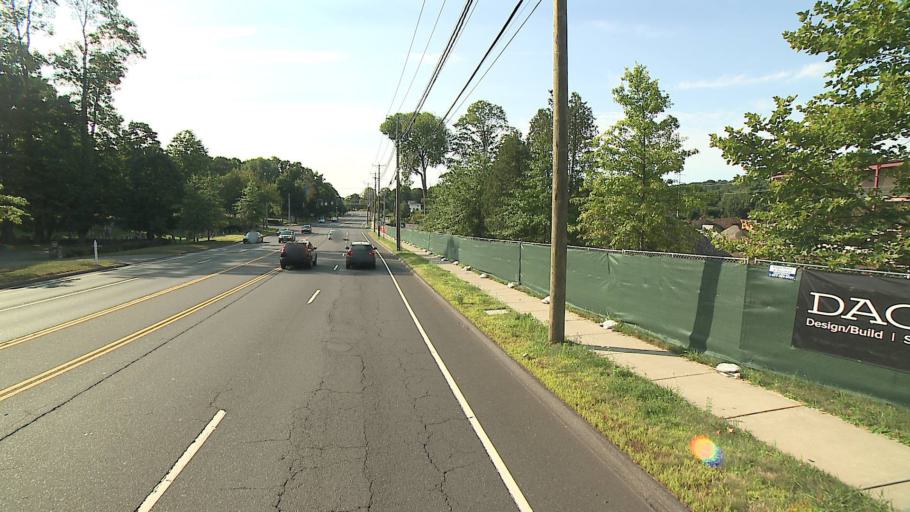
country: US
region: Connecticut
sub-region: Fairfield County
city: Wilton
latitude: 41.1910
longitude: -73.4278
